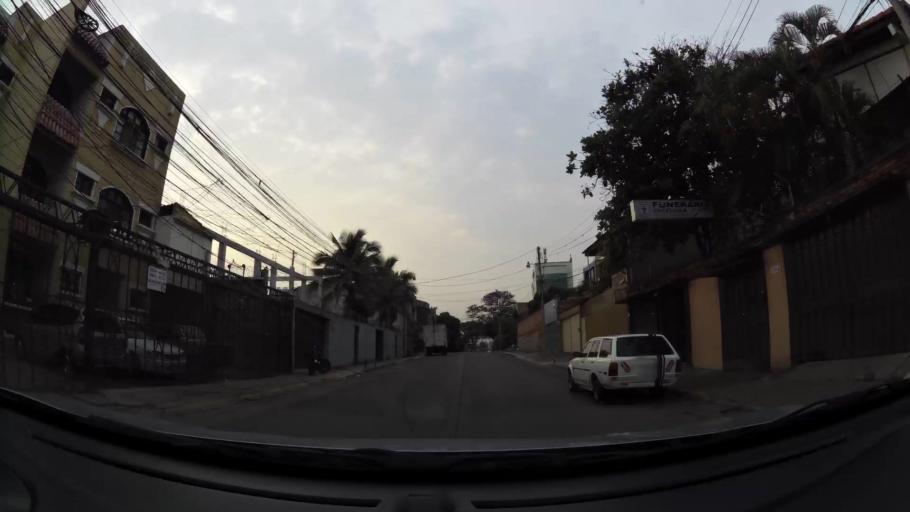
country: HN
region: Francisco Morazan
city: Tegucigalpa
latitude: 14.0913
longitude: -87.1952
